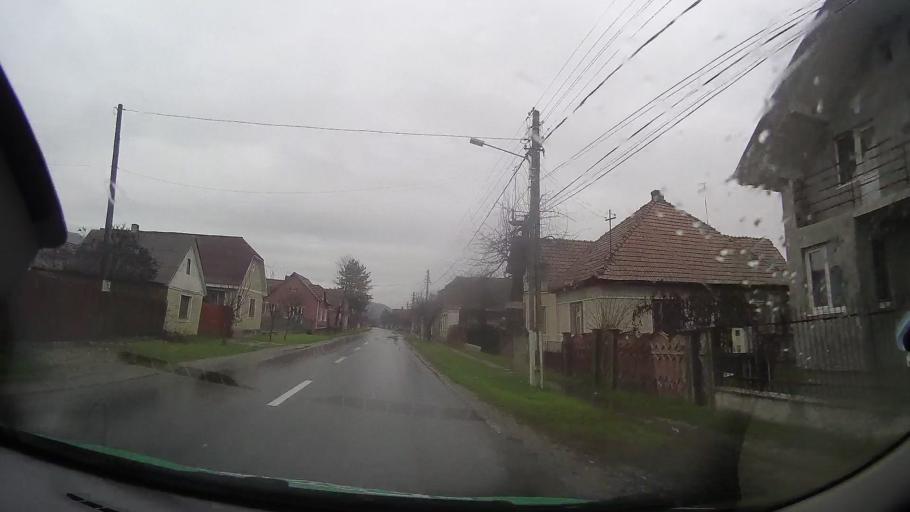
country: RO
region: Bistrita-Nasaud
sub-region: Comuna Mariselu
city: Mariselu
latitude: 47.0327
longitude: 24.4818
